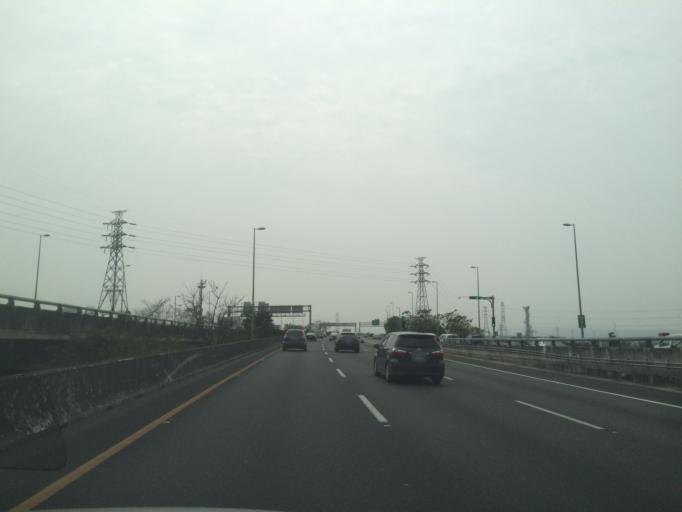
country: TW
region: Taiwan
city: Zhongxing New Village
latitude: 24.0445
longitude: 120.6789
